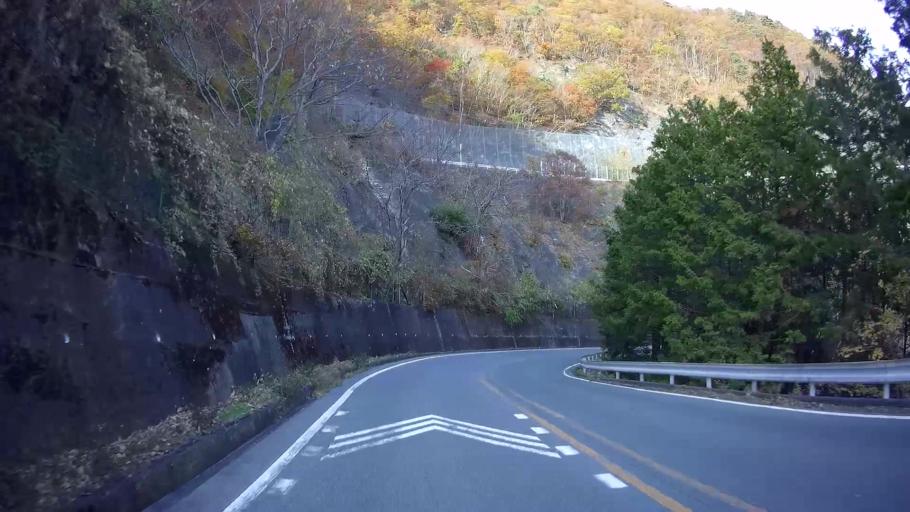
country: JP
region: Yamanashi
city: Fujikawaguchiko
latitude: 35.4785
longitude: 138.5504
